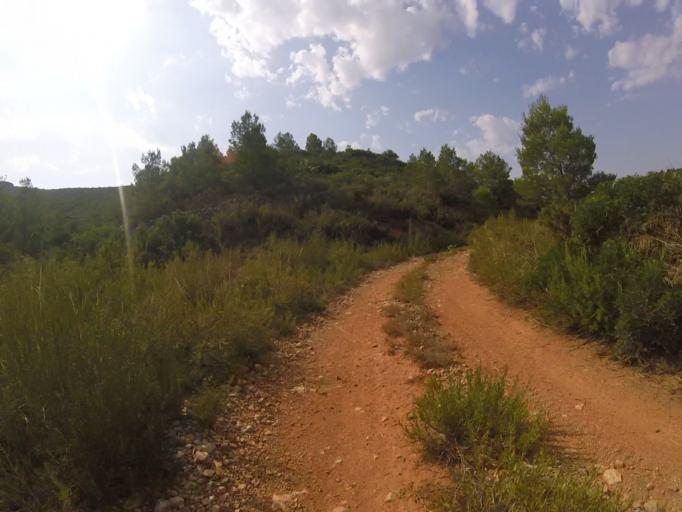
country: ES
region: Valencia
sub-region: Provincia de Castello
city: Alcala de Xivert
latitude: 40.3497
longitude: 0.1990
